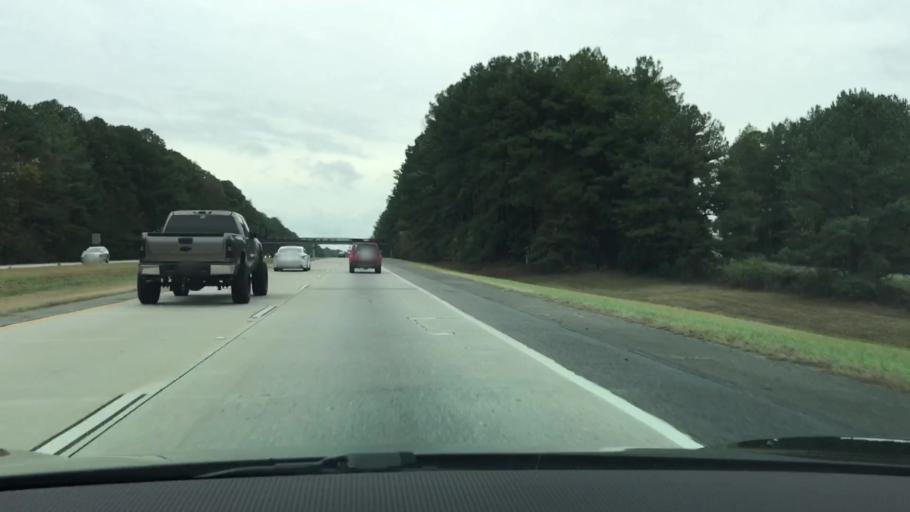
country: US
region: Georgia
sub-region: Greene County
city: Union Point
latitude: 33.5410
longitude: -83.0121
